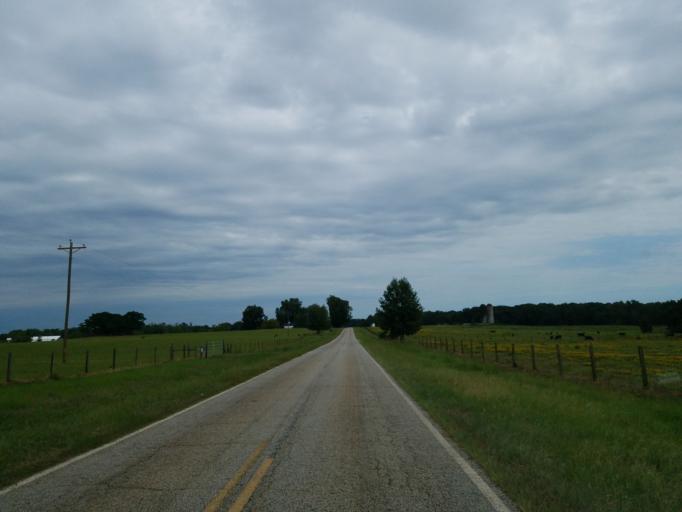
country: US
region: Georgia
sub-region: Lamar County
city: Barnesville
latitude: 33.0000
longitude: -84.0566
